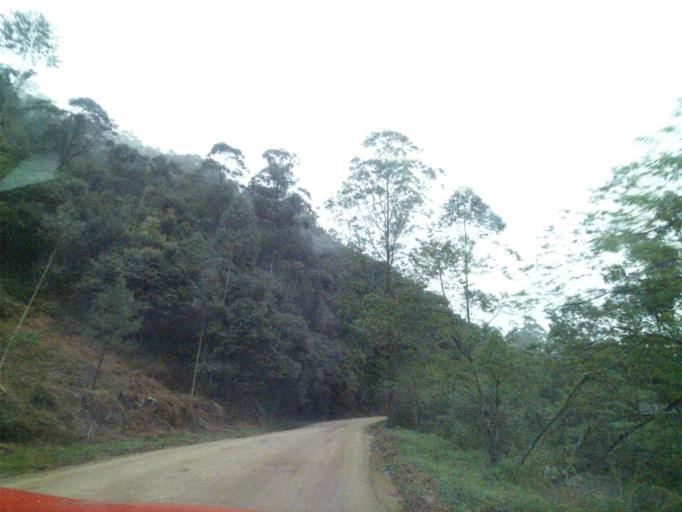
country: BR
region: Santa Catarina
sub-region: Anitapolis
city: Anitapolis
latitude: -27.9039
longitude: -49.1253
